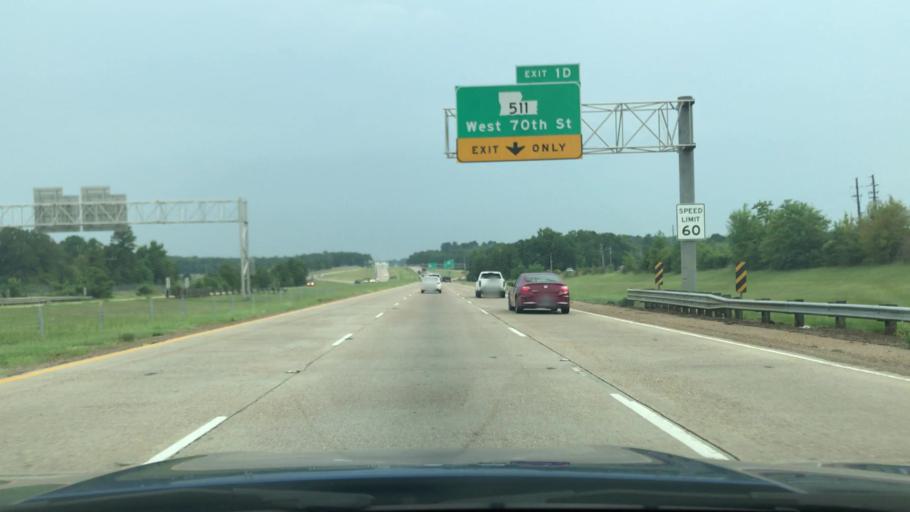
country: US
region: Louisiana
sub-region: Caddo Parish
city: Shreveport
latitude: 32.4492
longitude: -93.8433
